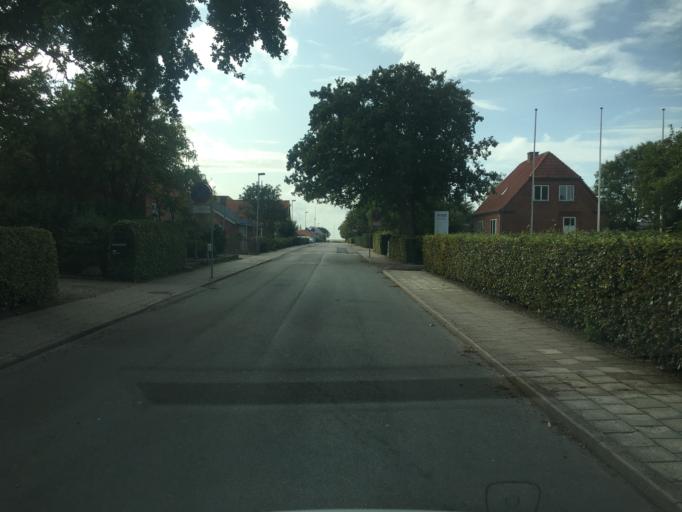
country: DE
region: Schleswig-Holstein
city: Rodenas
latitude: 54.9650
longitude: 8.6919
